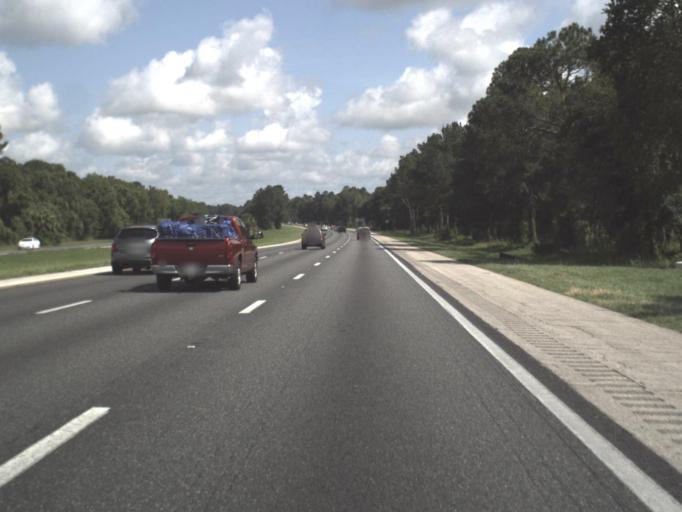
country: US
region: Florida
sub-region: Alachua County
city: Gainesville
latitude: 29.5068
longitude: -82.2990
